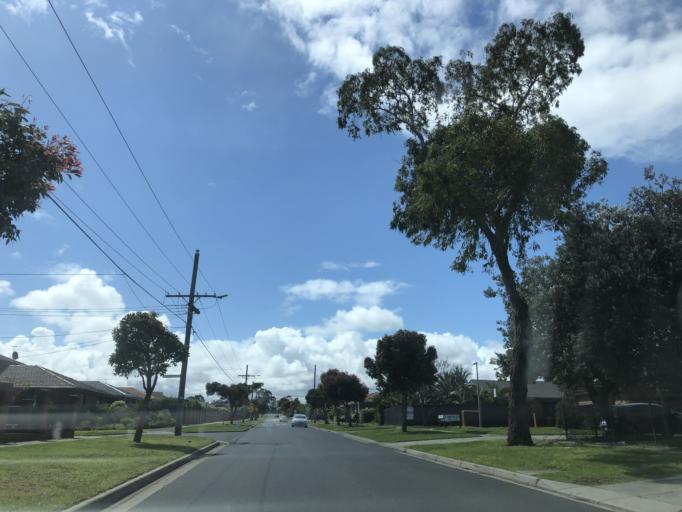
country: AU
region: Victoria
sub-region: Kingston
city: Clayton South
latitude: -37.9375
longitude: 145.1025
